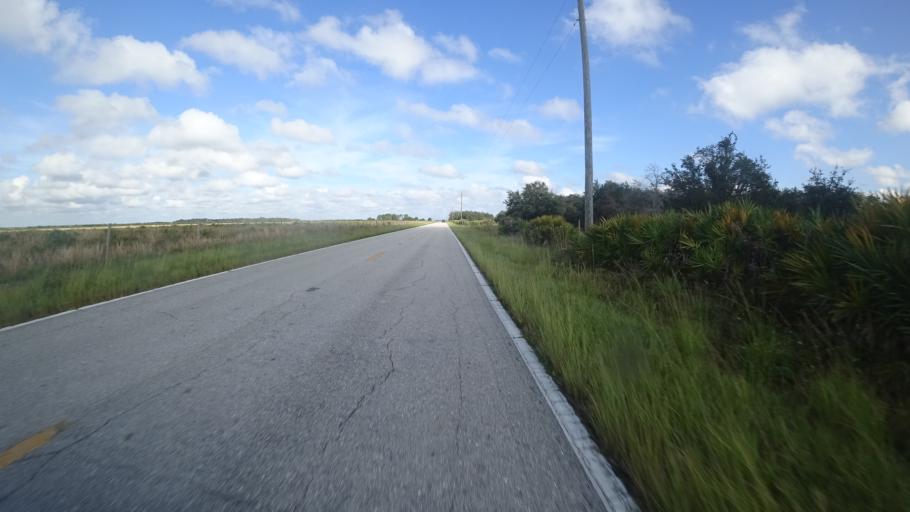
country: US
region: Florida
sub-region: Hardee County
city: Wauchula
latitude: 27.5077
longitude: -82.0718
